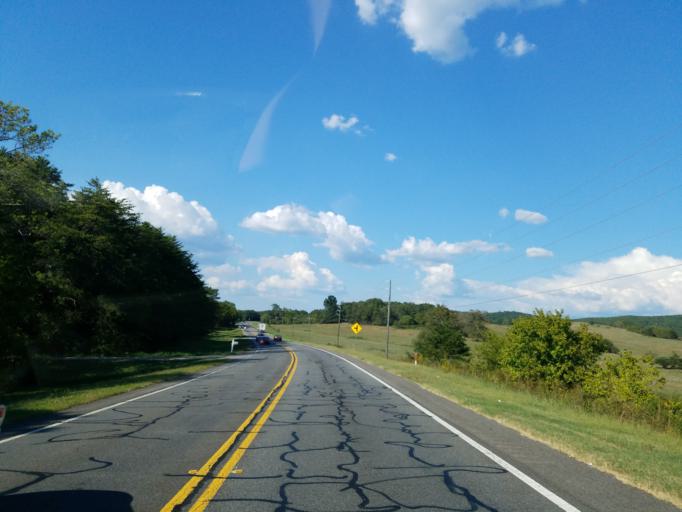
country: US
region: Georgia
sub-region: Bartow County
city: Rydal
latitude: 34.3754
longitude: -84.7096
